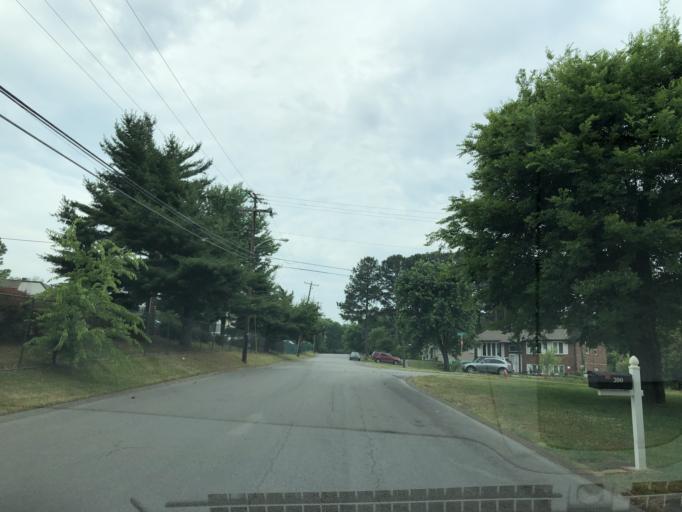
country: US
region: Tennessee
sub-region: Davidson County
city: Oak Hill
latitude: 36.0738
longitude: -86.6867
